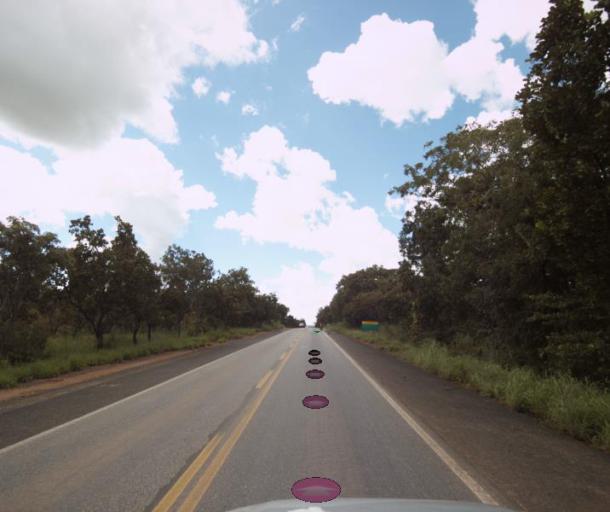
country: BR
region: Goias
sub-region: Porangatu
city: Porangatu
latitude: -13.7764
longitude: -49.0315
